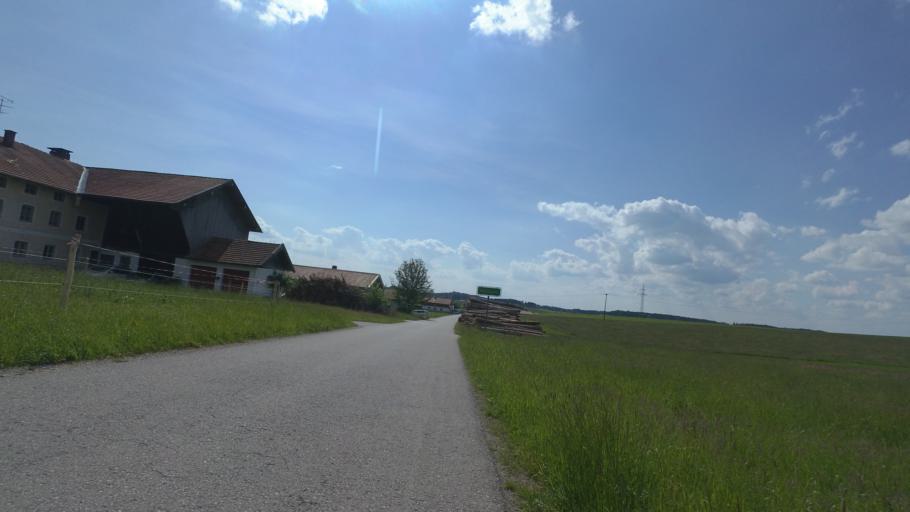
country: DE
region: Bavaria
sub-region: Upper Bavaria
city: Vachendorf
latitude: 47.8639
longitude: 12.5959
